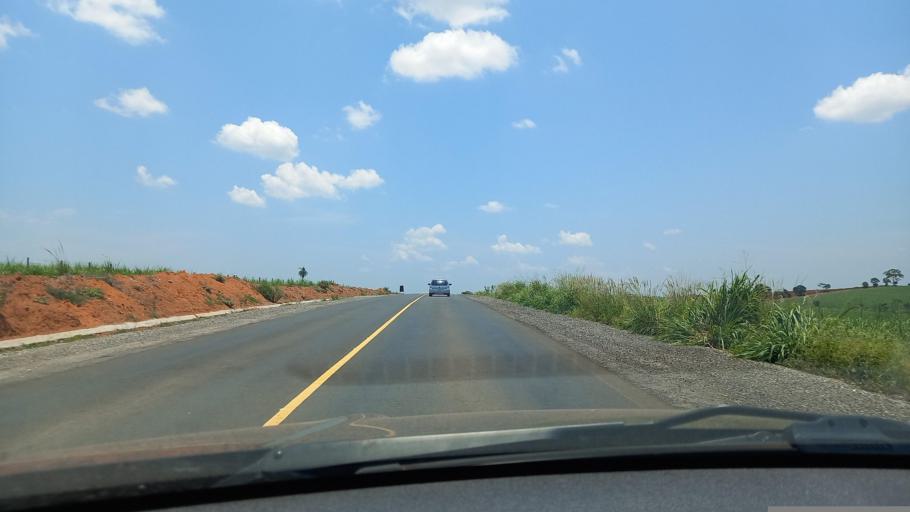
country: BR
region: Sao Paulo
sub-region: Moji-Guacu
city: Mogi-Gaucu
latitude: -22.3634
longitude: -46.8707
